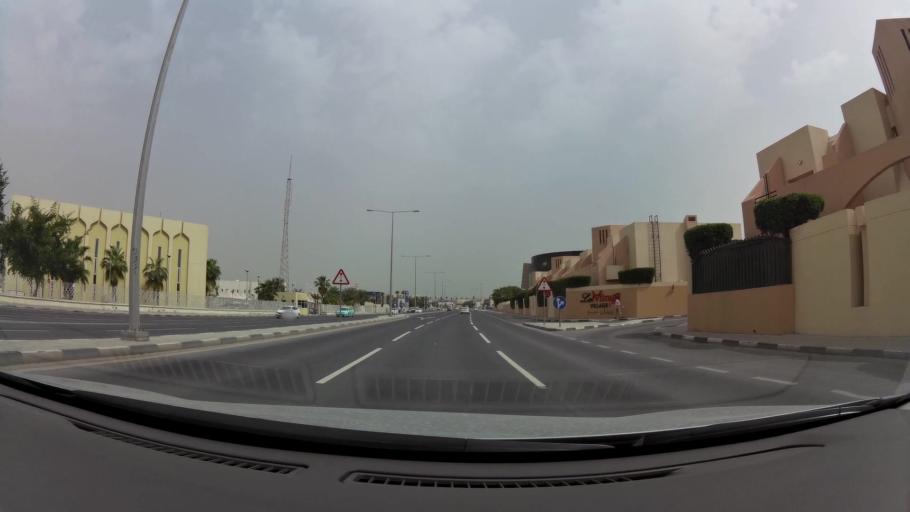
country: QA
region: Baladiyat ad Dawhah
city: Doha
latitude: 25.2567
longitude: 51.5367
